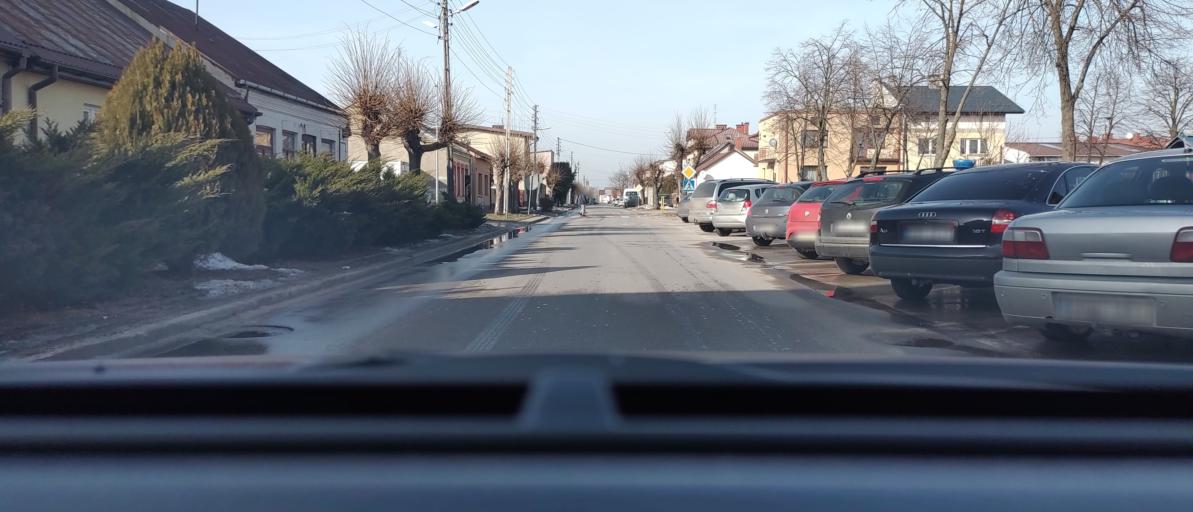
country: PL
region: Masovian Voivodeship
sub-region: Powiat bialobrzeski
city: Bialobrzegi
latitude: 51.6481
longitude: 20.9525
